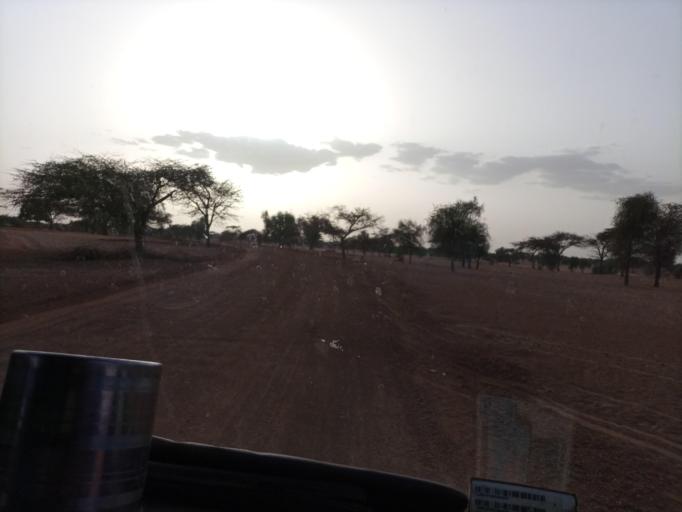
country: SN
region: Louga
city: Dara
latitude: 15.3687
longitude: -15.5697
